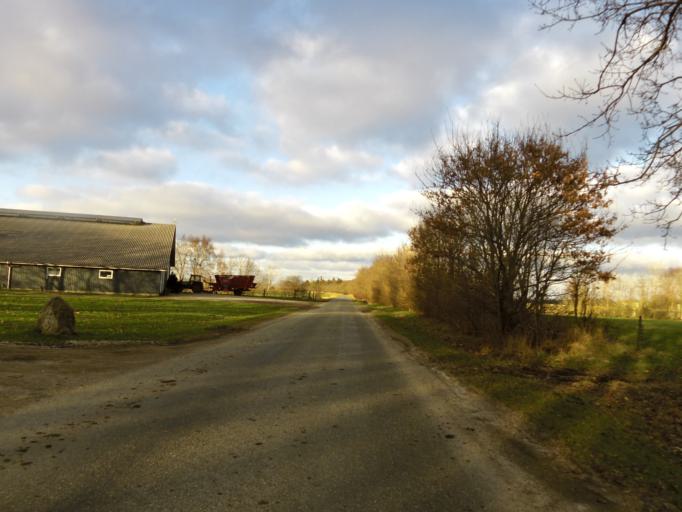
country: DK
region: South Denmark
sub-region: Esbjerg Kommune
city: Ribe
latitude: 55.2934
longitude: 8.8480
